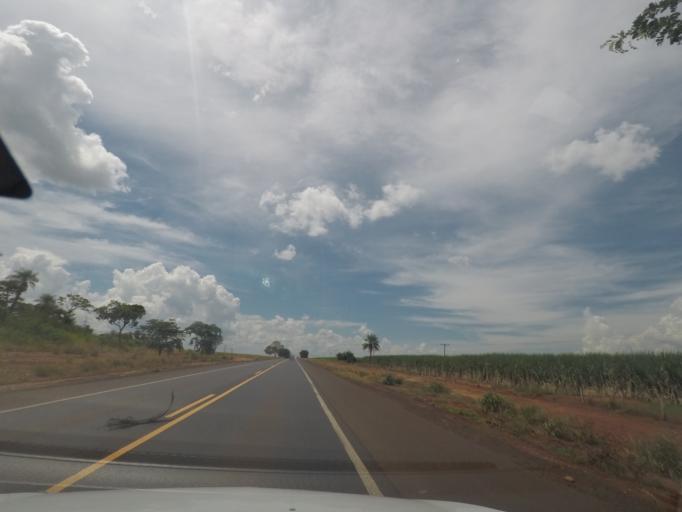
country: BR
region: Sao Paulo
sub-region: Barretos
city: Barretos
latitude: -20.2821
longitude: -48.6710
